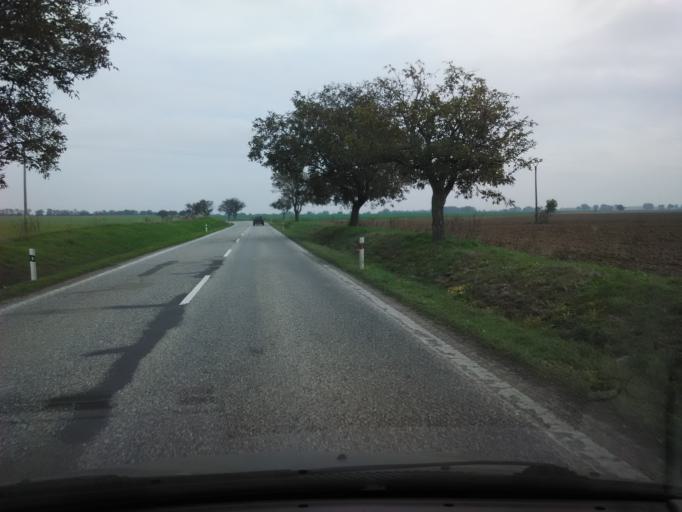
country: SK
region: Nitriansky
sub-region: Okres Nove Zamky
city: Nove Zamky
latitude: 47.9931
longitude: 18.2967
